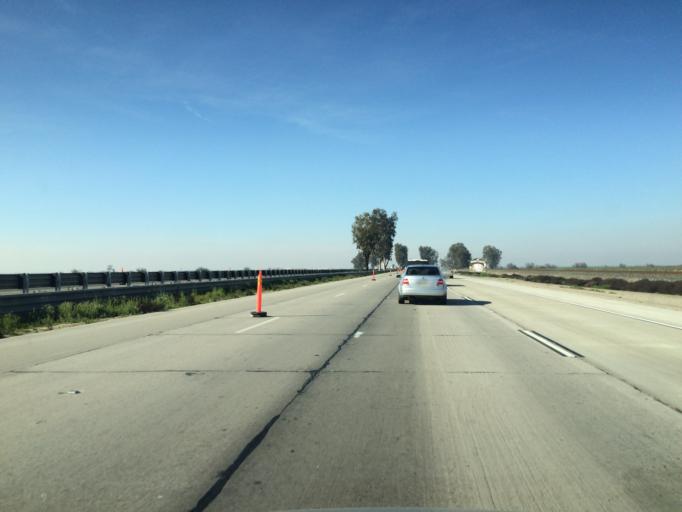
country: US
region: California
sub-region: Tulare County
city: Goshen
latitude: 36.3982
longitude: -119.4522
